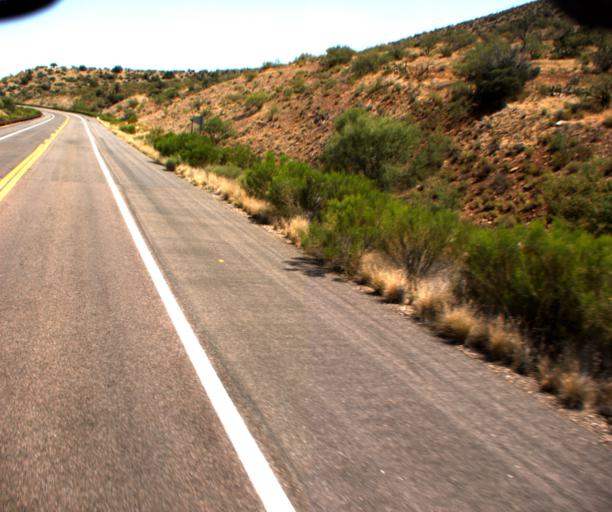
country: US
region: Arizona
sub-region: Gila County
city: Claypool
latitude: 33.4979
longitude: -110.8662
